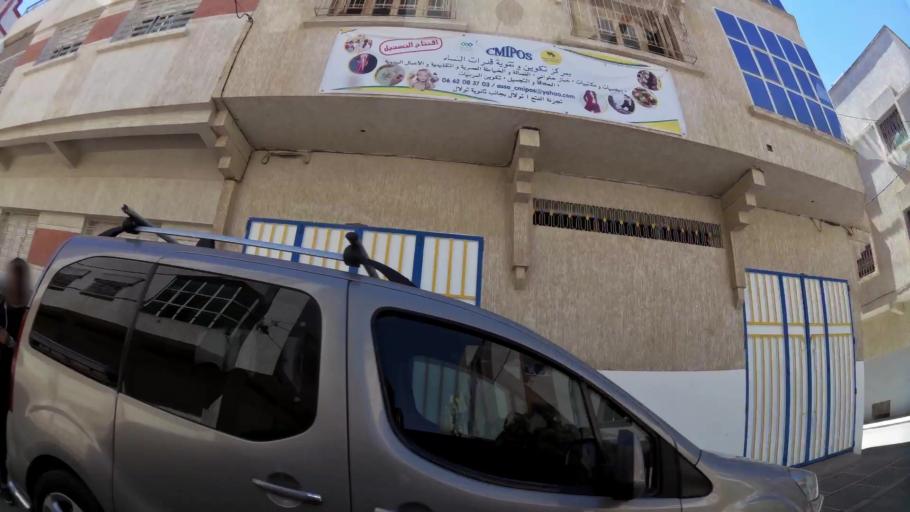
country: MA
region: Meknes-Tafilalet
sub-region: Meknes
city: Meknes
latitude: 33.8960
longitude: -5.5796
